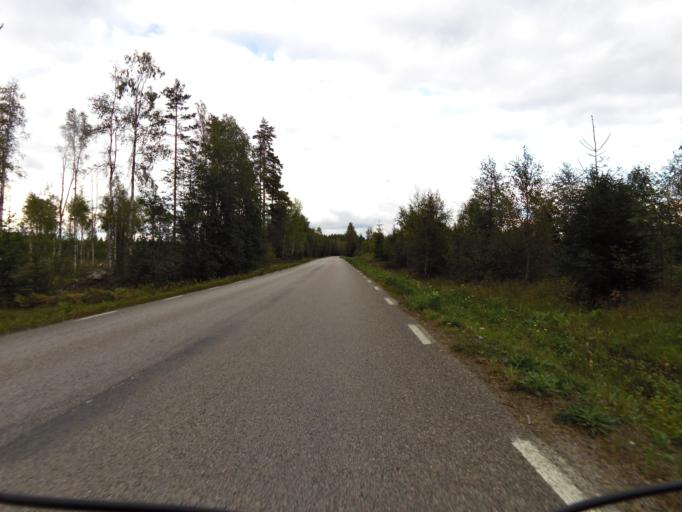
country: SE
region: Gaevleborg
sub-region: Sandvikens Kommun
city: Sandviken
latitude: 60.6491
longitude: 16.8228
